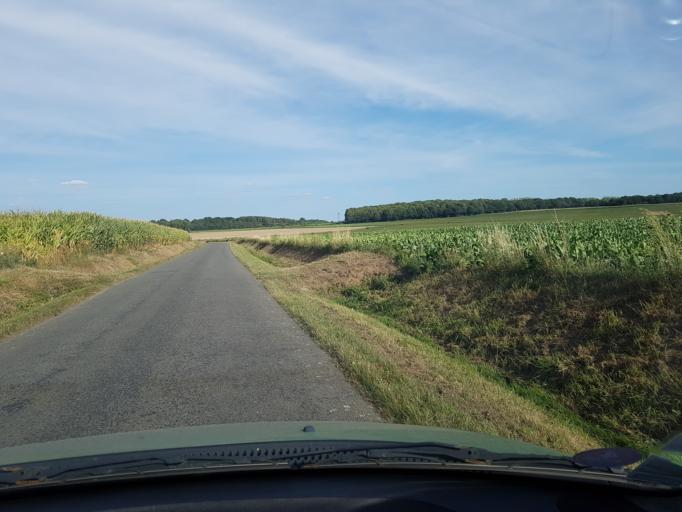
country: FR
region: Nord-Pas-de-Calais
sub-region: Departement du Pas-de-Calais
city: Labeuvriere
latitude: 50.5259
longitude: 2.5736
